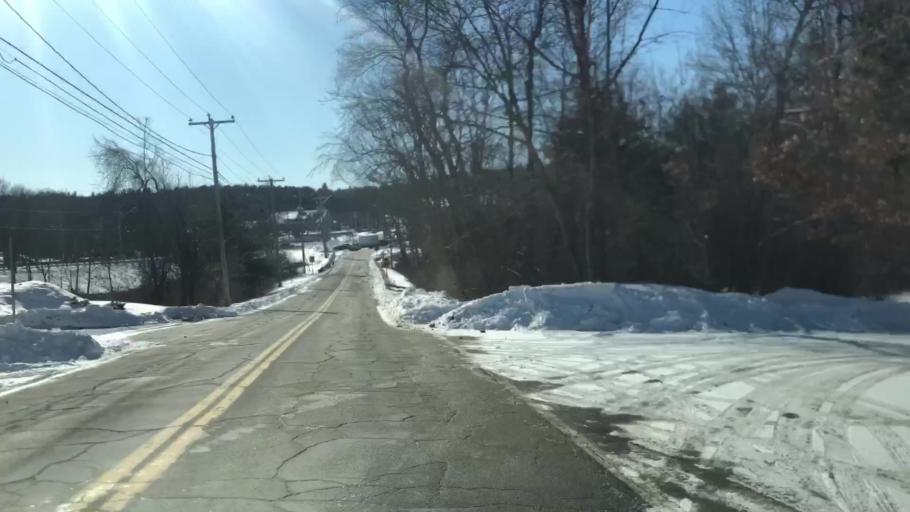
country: US
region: New Hampshire
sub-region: Hillsborough County
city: Bedford
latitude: 42.9400
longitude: -71.5238
